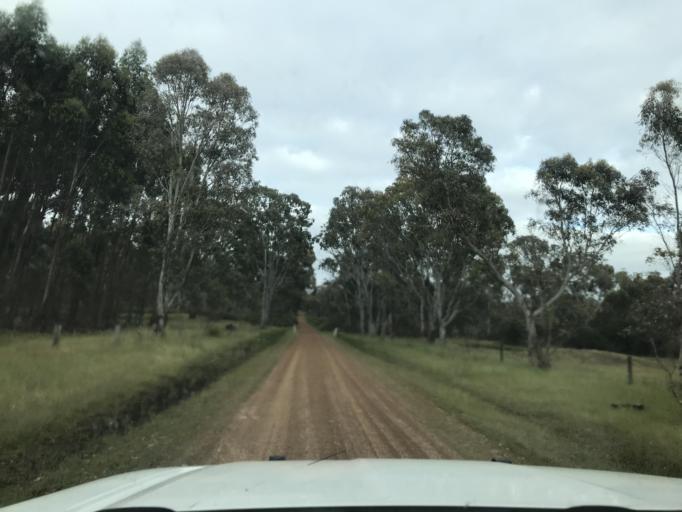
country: AU
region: South Australia
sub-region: Wattle Range
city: Penola
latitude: -37.2795
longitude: 141.3872
